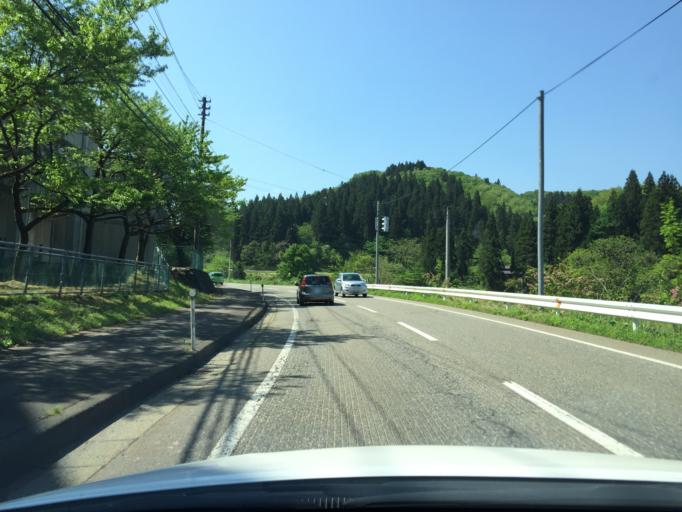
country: JP
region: Niigata
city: Kamo
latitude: 37.6144
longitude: 139.1023
